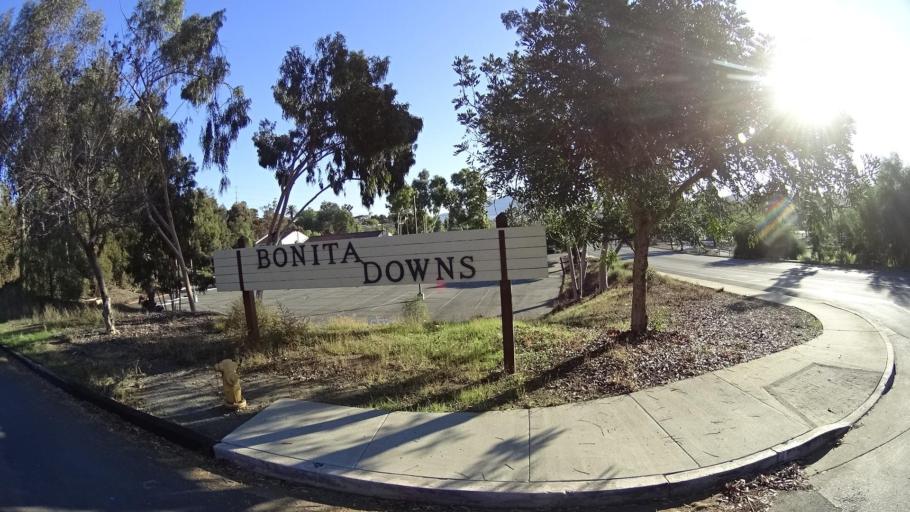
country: US
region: California
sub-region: San Diego County
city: Bonita
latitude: 32.6673
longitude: -117.0288
